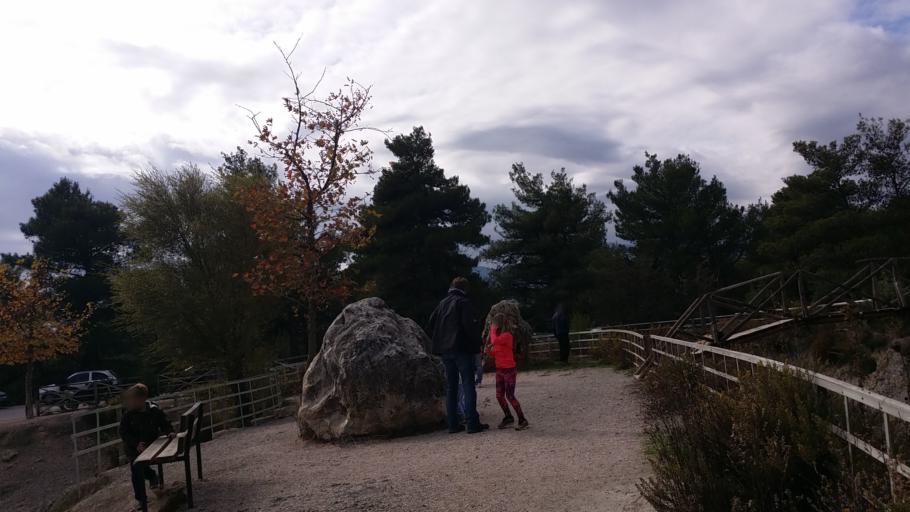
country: GR
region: Attica
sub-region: Nomarchia Anatolikis Attikis
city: Afidnes
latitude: 38.2130
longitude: 23.8044
